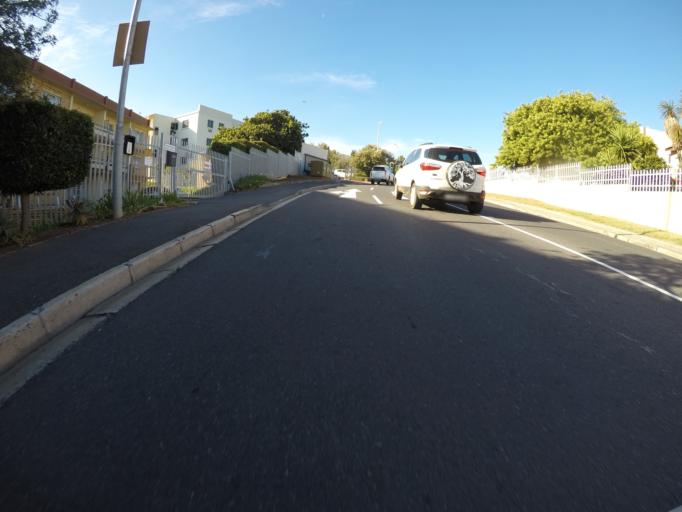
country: ZA
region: Western Cape
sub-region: City of Cape Town
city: Kraaifontein
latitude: -33.8805
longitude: 18.6444
